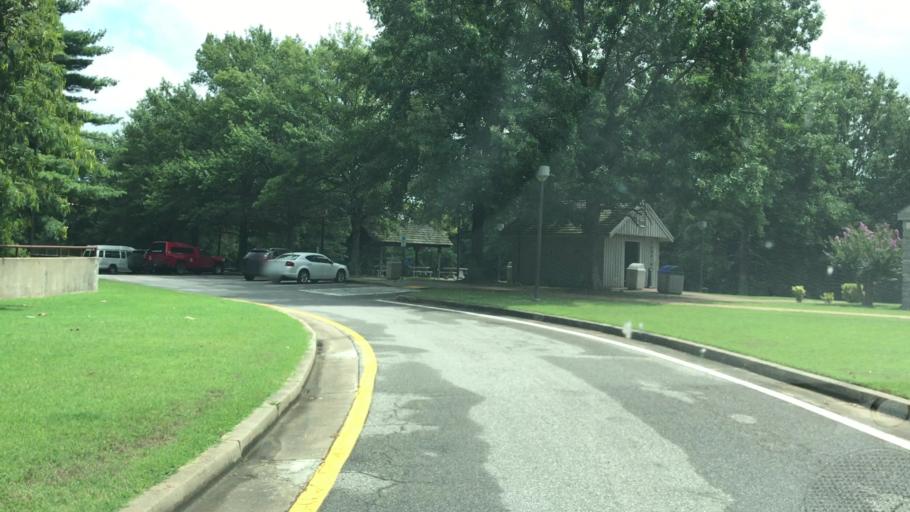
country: US
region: Tennessee
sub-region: Dyer County
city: Dyersburg
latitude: 36.0711
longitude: -89.4696
